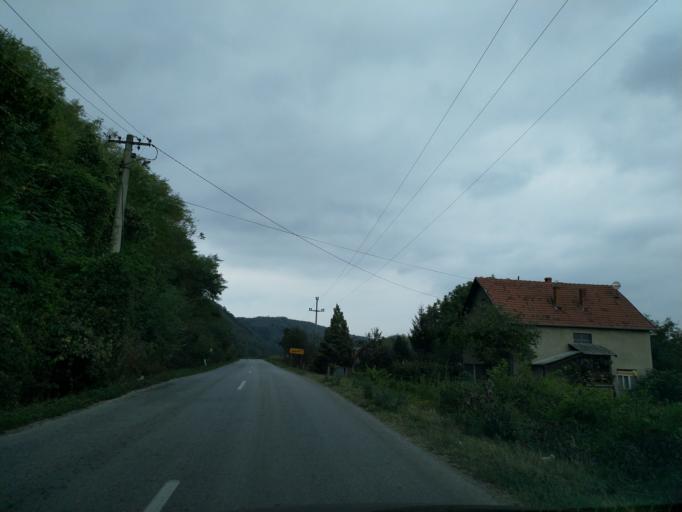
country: RS
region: Central Serbia
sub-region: Sumadijski Okrug
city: Batocina
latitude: 44.0837
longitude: 21.1776
